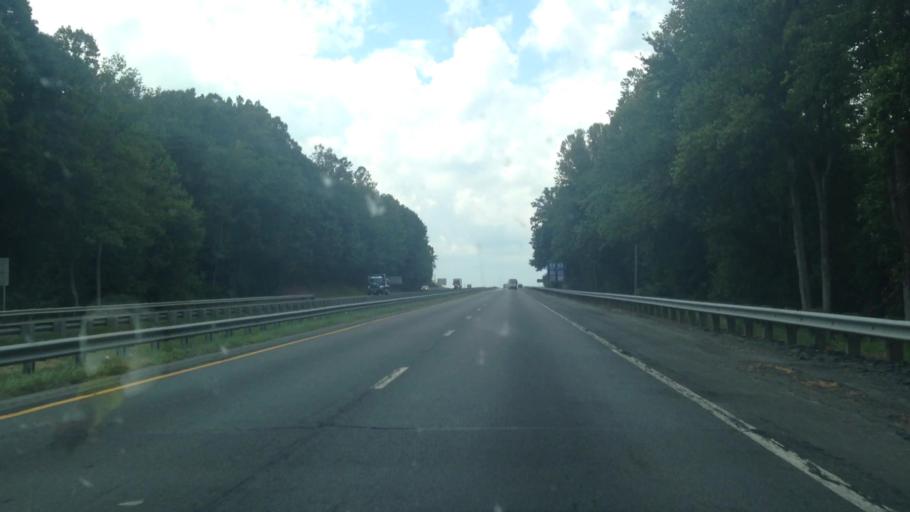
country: US
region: North Carolina
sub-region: Forsyth County
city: Tobaccoville
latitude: 36.2531
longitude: -80.3575
